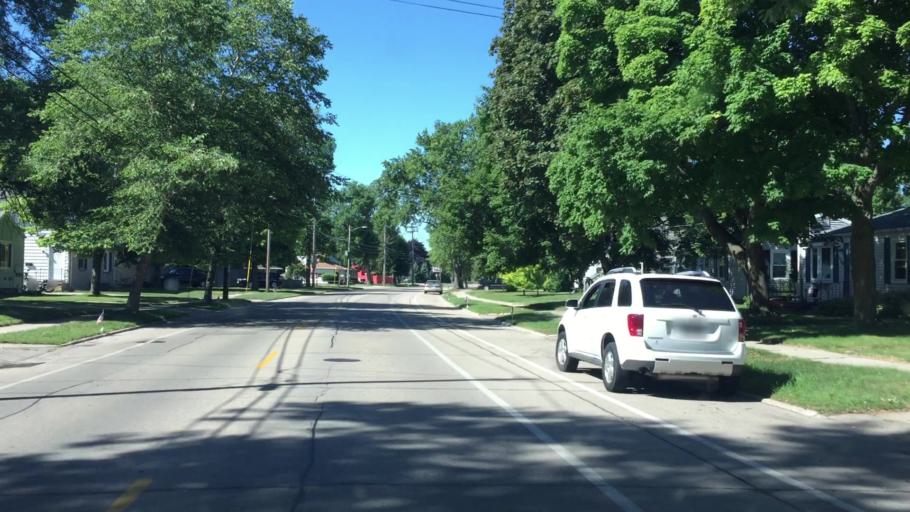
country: US
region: Wisconsin
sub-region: Winnebago County
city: Menasha
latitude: 44.2126
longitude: -88.4356
